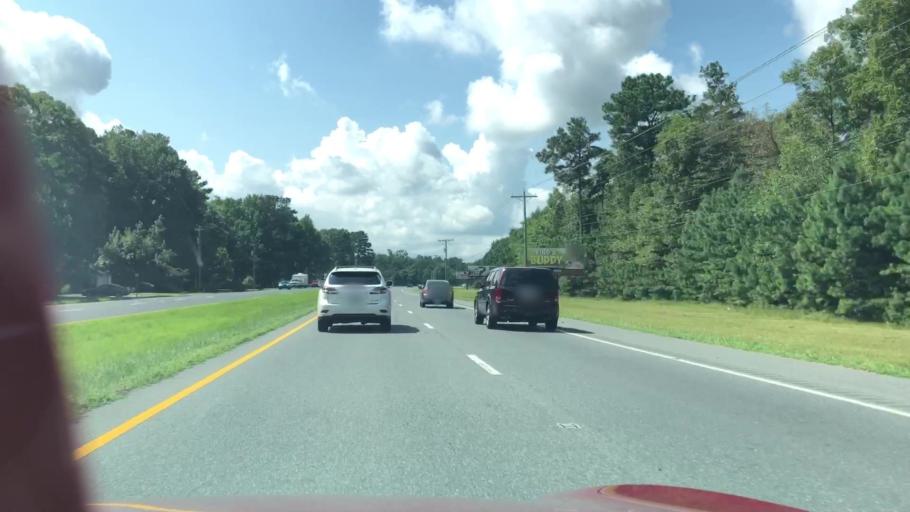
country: US
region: Virginia
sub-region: Accomack County
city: Wattsville
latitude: 37.8305
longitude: -75.5787
